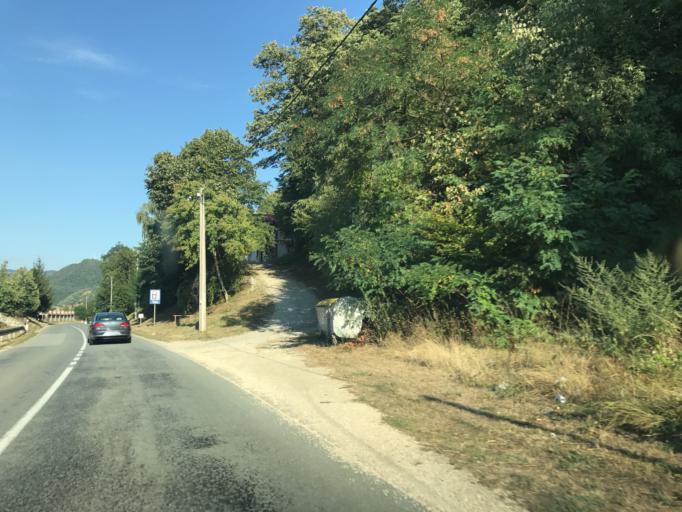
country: RO
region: Mehedinti
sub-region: Comuna Svinita
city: Svinita
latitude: 44.4646
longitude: 22.1342
